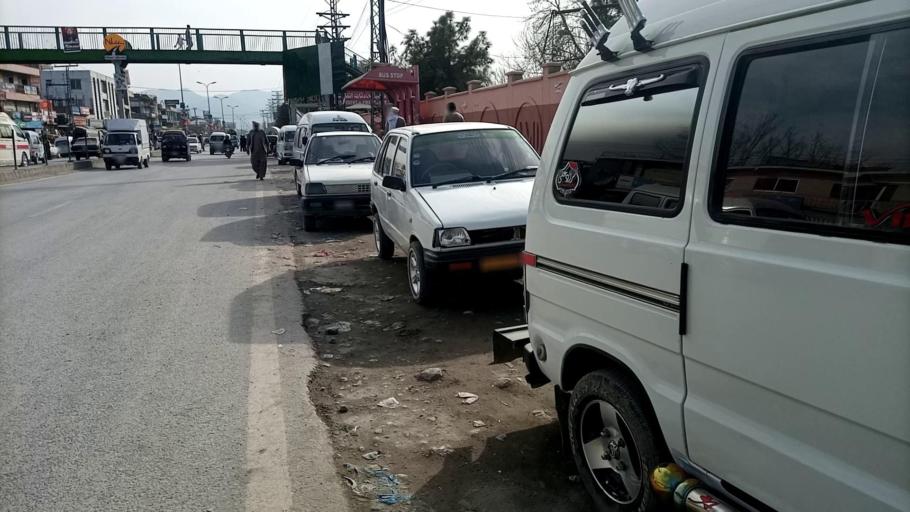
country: PK
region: Khyber Pakhtunkhwa
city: Abbottabad
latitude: 34.2035
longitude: 73.2391
